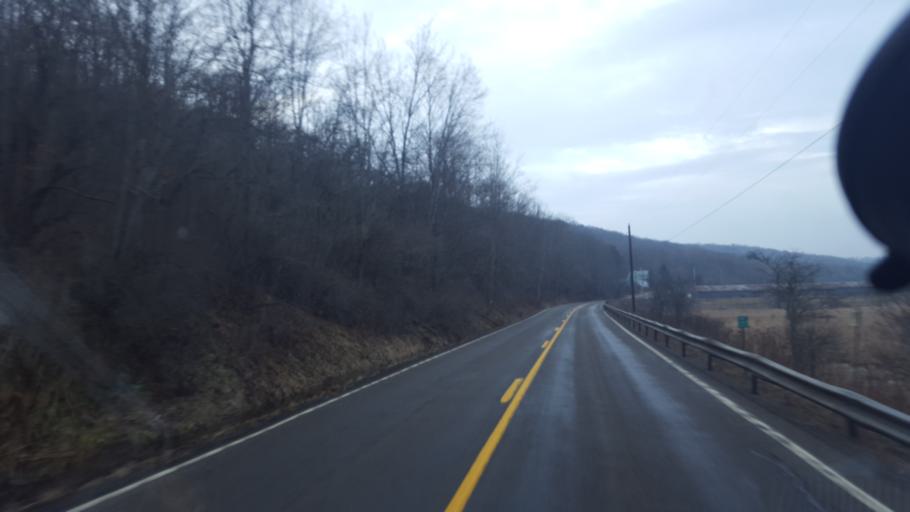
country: US
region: New York
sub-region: Allegany County
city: Andover
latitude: 42.0644
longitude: -77.7338
